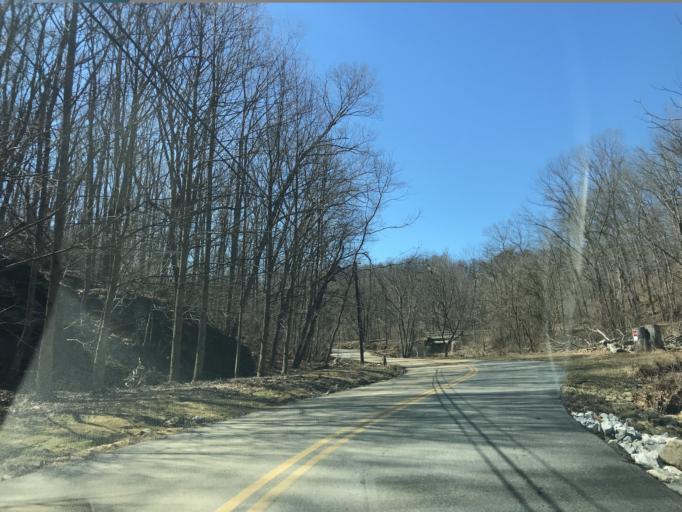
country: US
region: Pennsylvania
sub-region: York County
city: New Freedom
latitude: 39.6736
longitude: -76.6717
